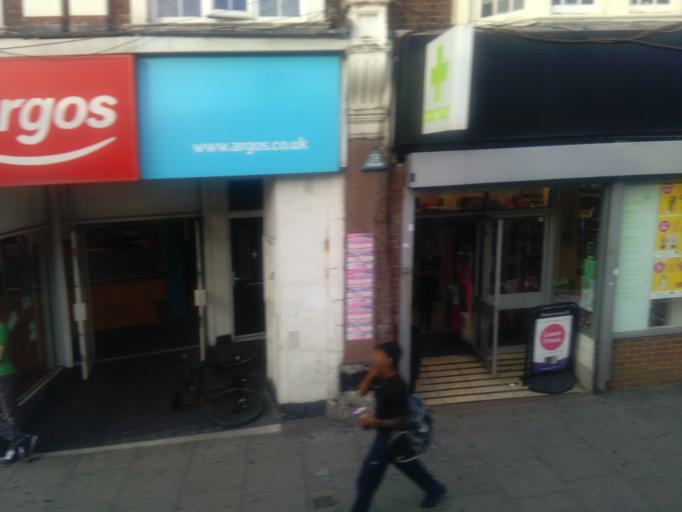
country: GB
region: England
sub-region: Greater London
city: Camberwell
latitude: 51.4855
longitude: -0.0938
